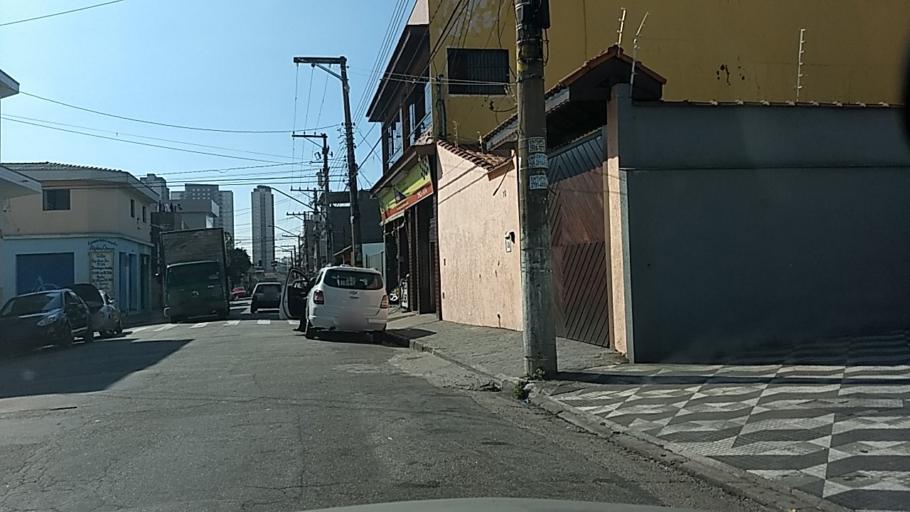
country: BR
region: Sao Paulo
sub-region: Guarulhos
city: Guarulhos
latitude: -23.4857
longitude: -46.5707
